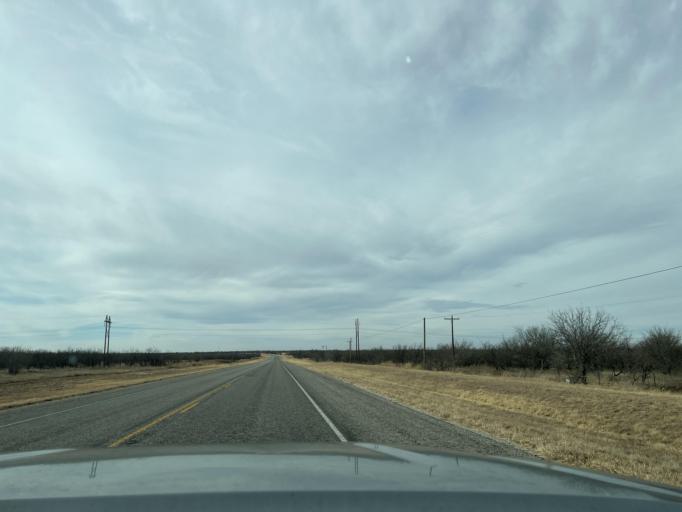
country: US
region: Texas
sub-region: Shackelford County
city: Albany
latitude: 32.7604
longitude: -99.5700
